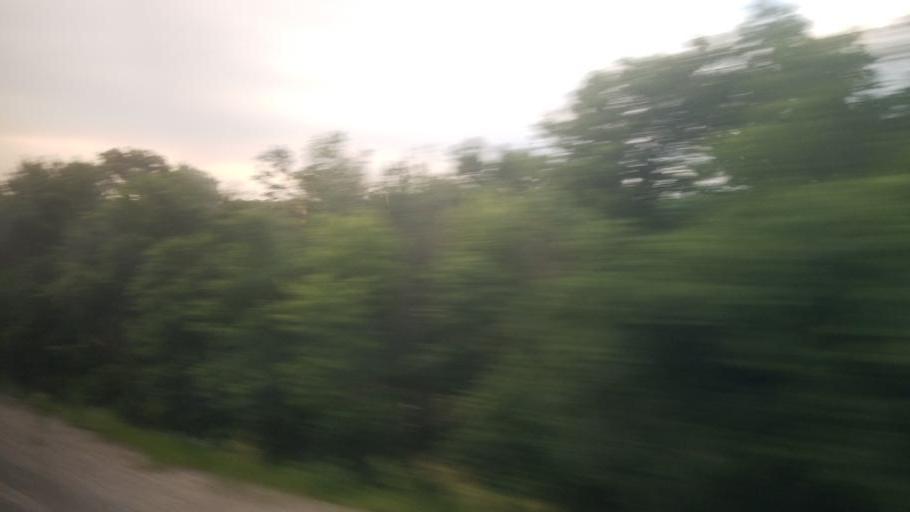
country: US
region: Kansas
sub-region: Marion County
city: Peabody
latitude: 38.1651
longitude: -97.0803
